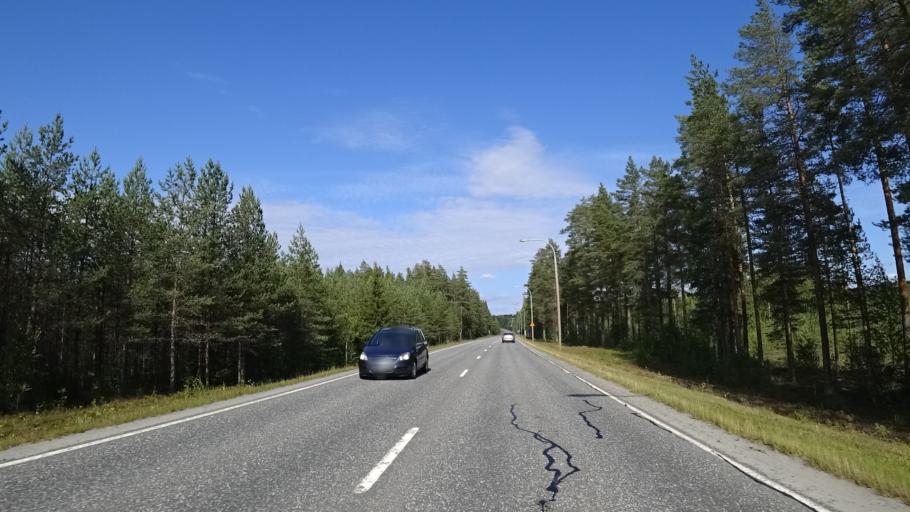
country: FI
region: North Karelia
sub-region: Joensuu
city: Eno
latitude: 62.7741
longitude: 30.0551
